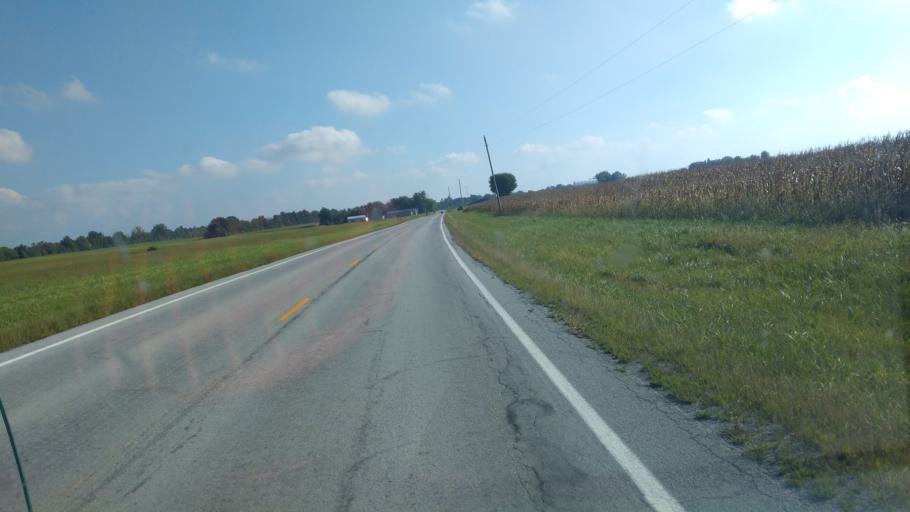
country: US
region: Ohio
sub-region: Hardin County
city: Forest
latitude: 40.8167
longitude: -83.5201
